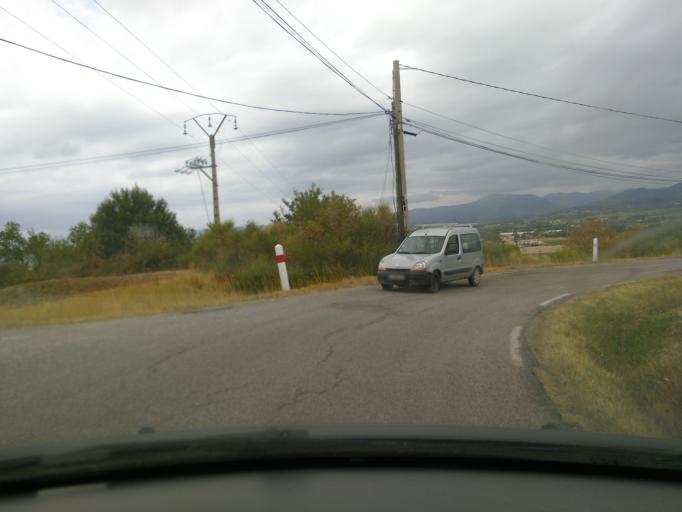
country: FR
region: Provence-Alpes-Cote d'Azur
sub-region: Departement du Vaucluse
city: Valreas
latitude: 44.3716
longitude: 5.0073
